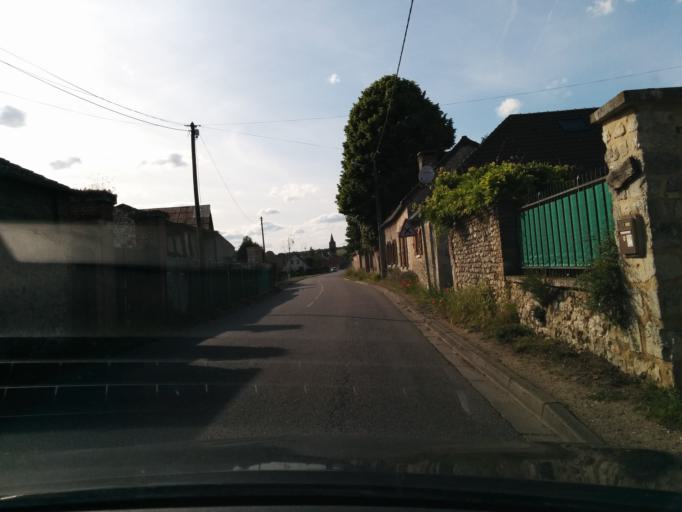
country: FR
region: Haute-Normandie
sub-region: Departement de l'Eure
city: Courcelles-sur-Seine
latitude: 49.1663
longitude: 1.4114
